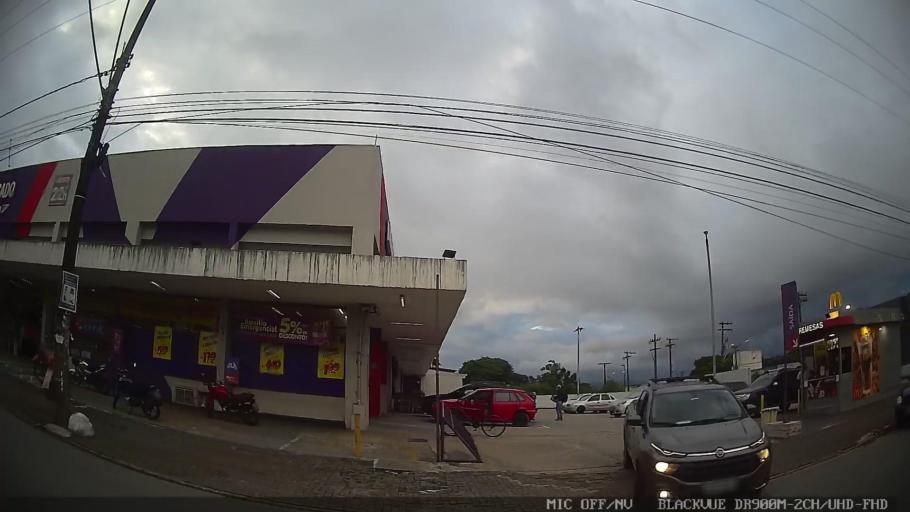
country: BR
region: Sao Paulo
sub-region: Itanhaem
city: Itanhaem
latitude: -24.1799
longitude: -46.7816
